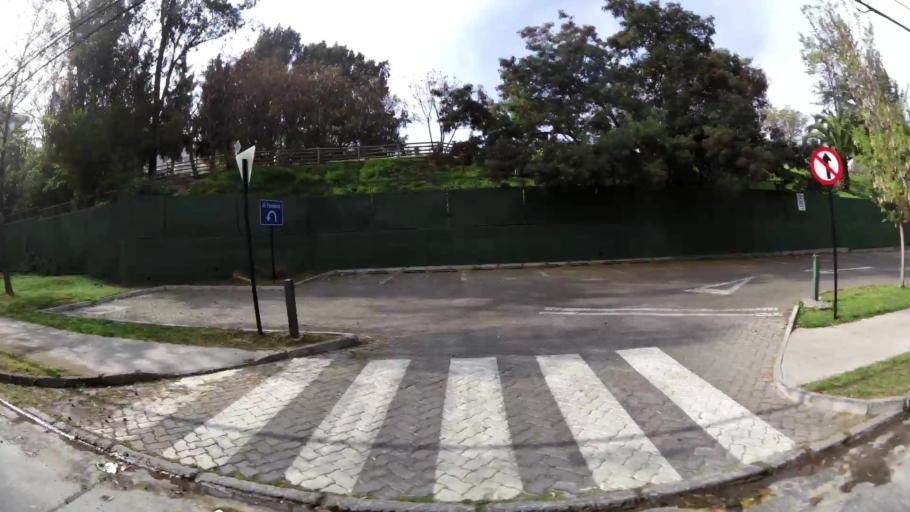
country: CL
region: Santiago Metropolitan
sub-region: Provincia de Santiago
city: Villa Presidente Frei, Nunoa, Santiago, Chile
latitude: -33.3749
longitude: -70.5274
